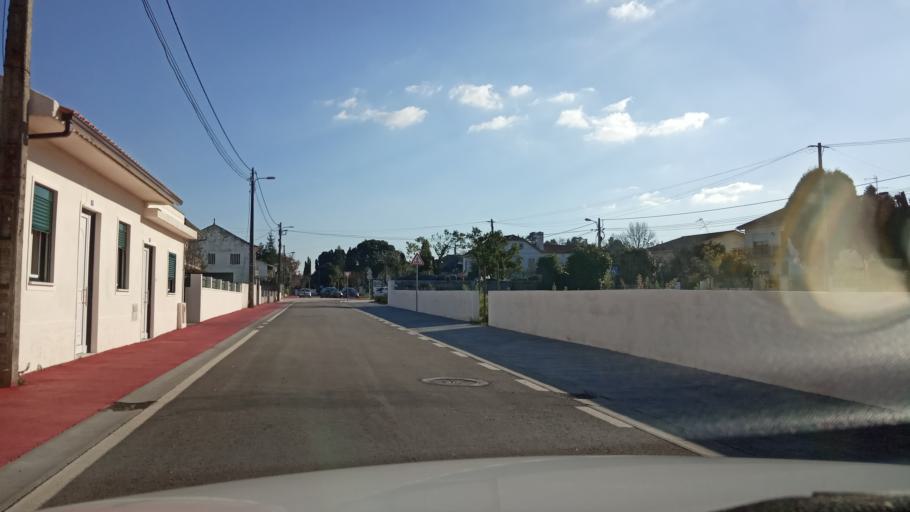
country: PT
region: Aveiro
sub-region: Anadia
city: Anadia
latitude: 40.4344
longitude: -8.4323
